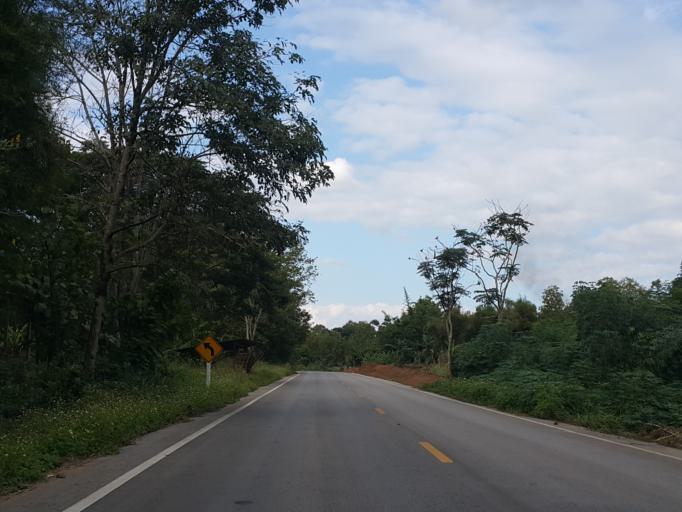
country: TH
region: Lampang
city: Chae Hom
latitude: 18.6407
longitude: 99.4939
